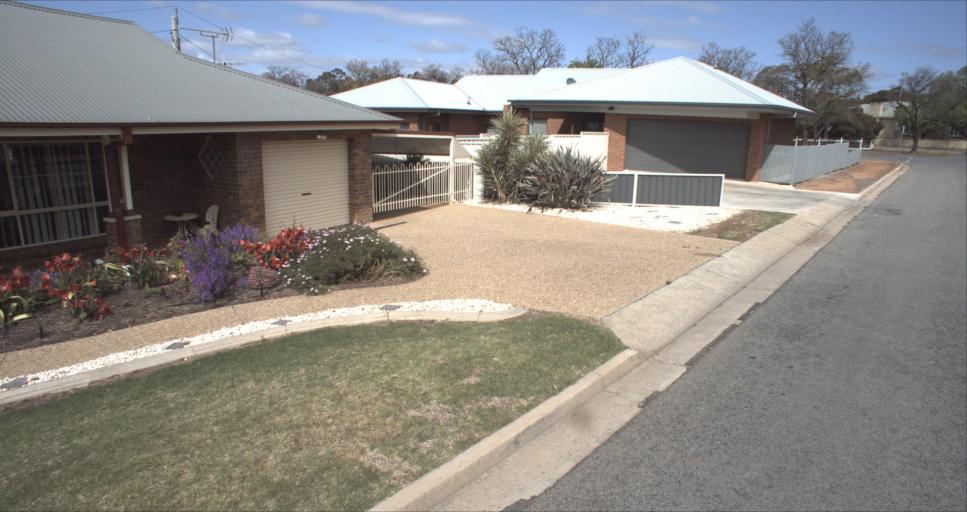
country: AU
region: New South Wales
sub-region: Leeton
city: Leeton
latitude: -34.5559
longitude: 146.4048
